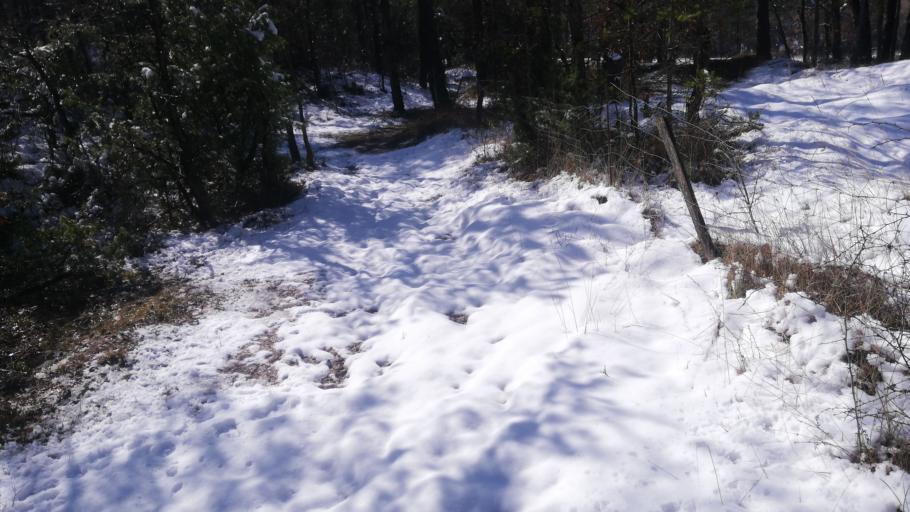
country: FR
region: Provence-Alpes-Cote d'Azur
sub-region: Departement des Alpes-de-Haute-Provence
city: Digne-les-Bains
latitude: 44.0449
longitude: 6.1988
